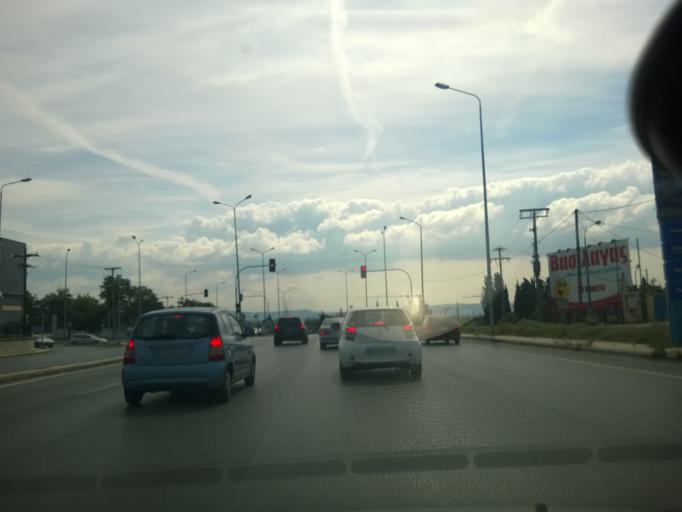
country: GR
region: Central Macedonia
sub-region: Nomos Thessalonikis
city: Kalamaria
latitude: 40.5595
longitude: 22.9770
